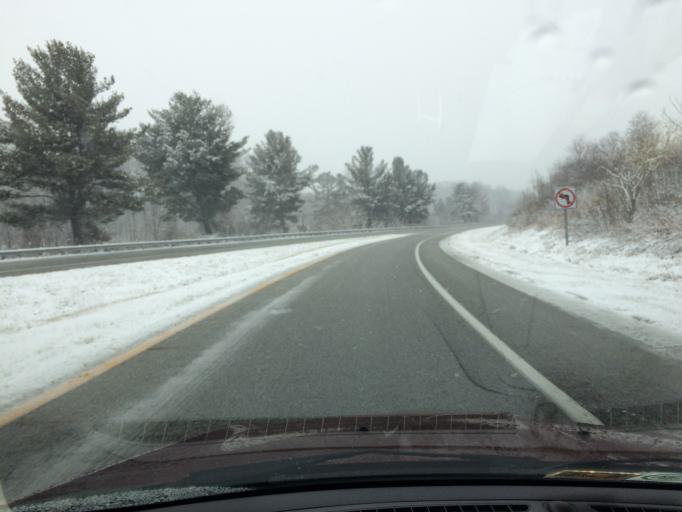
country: US
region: Virginia
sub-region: Amherst County
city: Amherst
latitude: 37.5631
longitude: -79.0619
